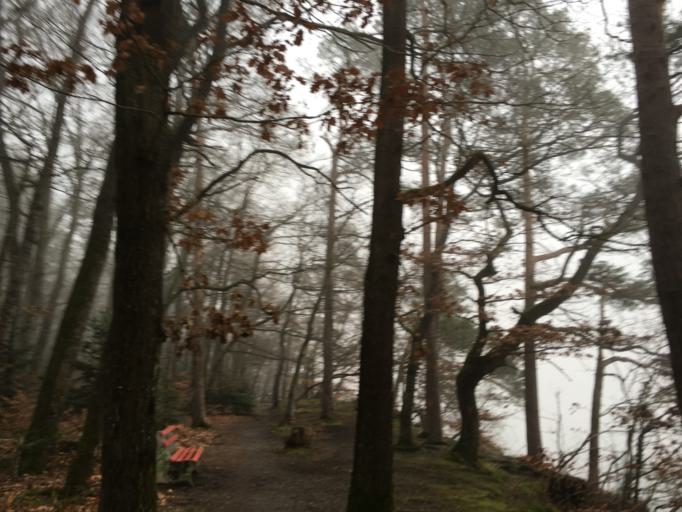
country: CH
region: Aargau
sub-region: Bezirk Zurzach
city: Koblenz
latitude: 47.6136
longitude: 8.2626
